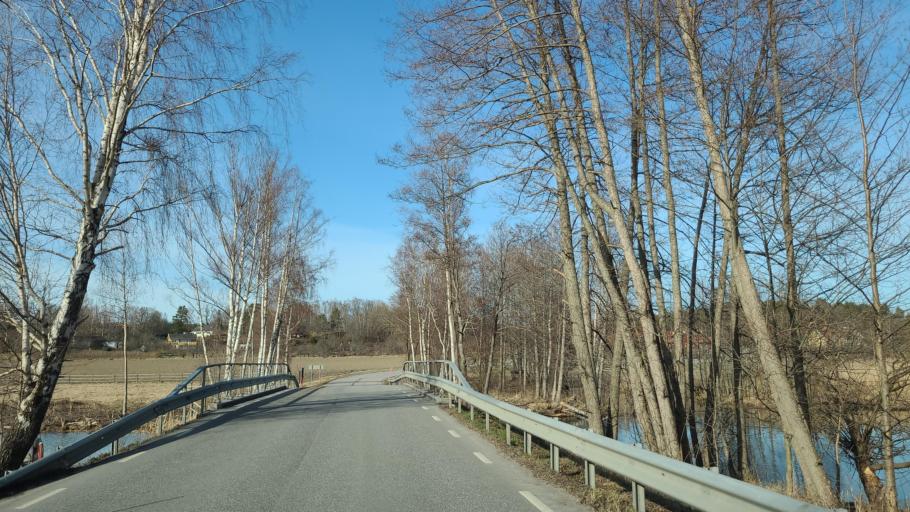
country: SE
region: Stockholm
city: Stenhamra
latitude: 59.2789
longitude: 17.7079
